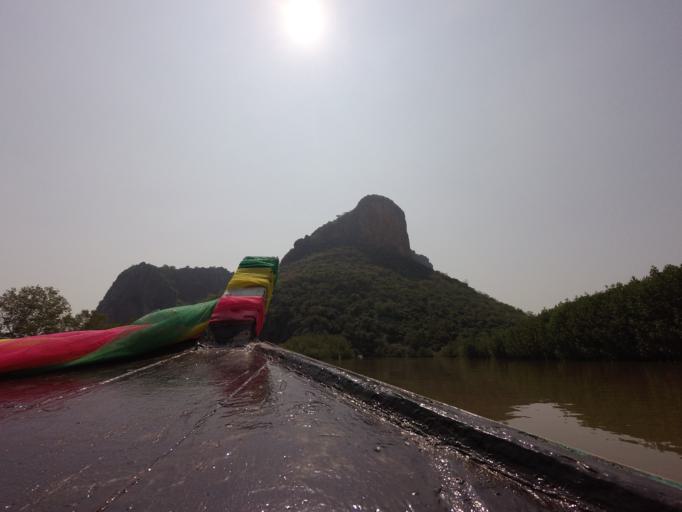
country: TH
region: Prachuap Khiri Khan
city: Kui Buri
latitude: 12.1436
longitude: 99.9521
